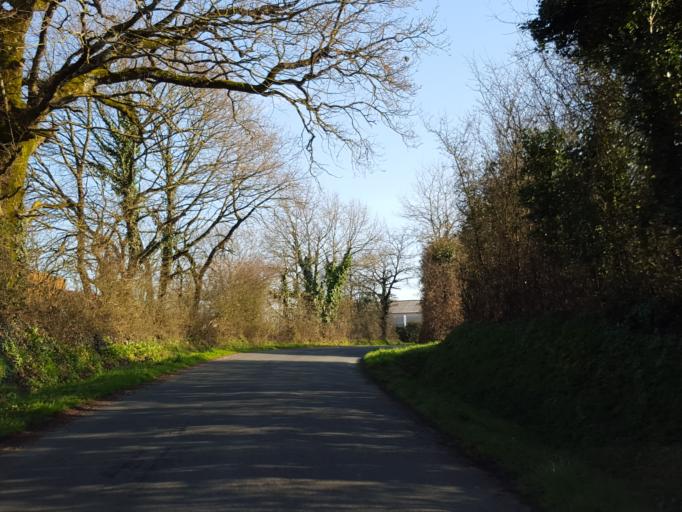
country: FR
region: Pays de la Loire
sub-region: Departement de la Vendee
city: La Chaize-le-Vicomte
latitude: 46.6723
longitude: -1.2849
